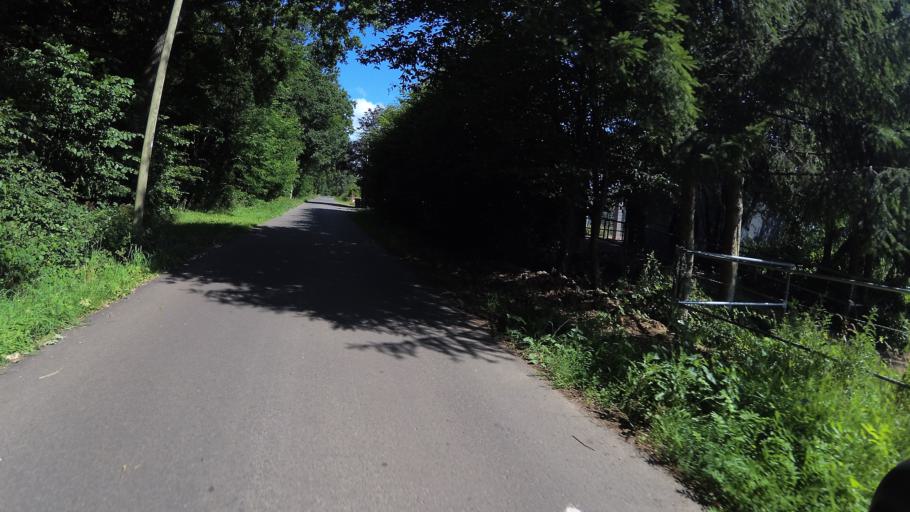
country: DE
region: Saarland
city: Weiskirchen
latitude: 49.5066
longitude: 6.8211
